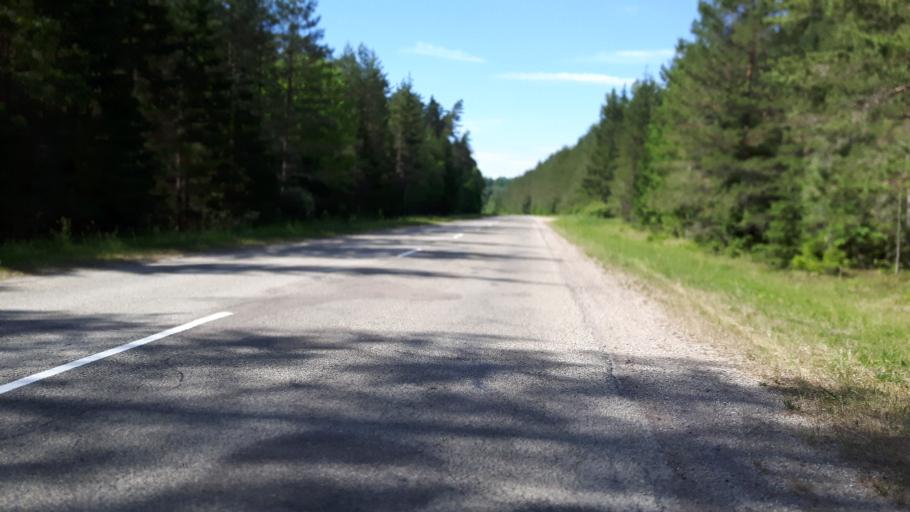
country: LV
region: Talsu Rajons
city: Sabile
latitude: 57.0771
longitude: 22.5307
